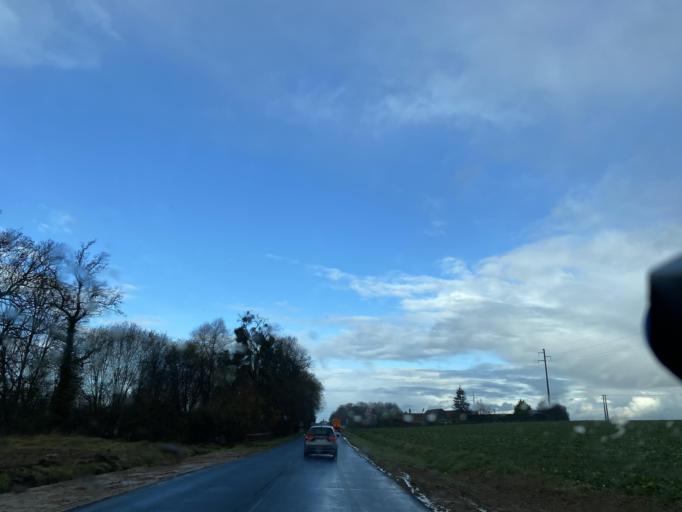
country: FR
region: Centre
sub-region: Departement d'Eure-et-Loir
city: Chateauneuf-en-Thymerais
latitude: 48.5659
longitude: 1.2538
